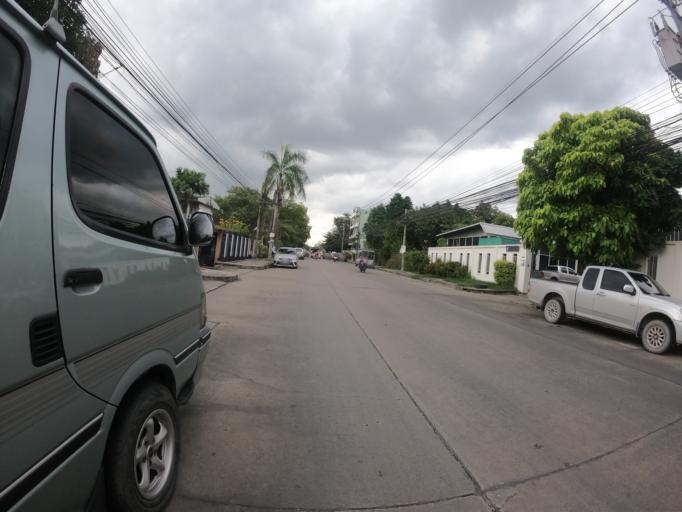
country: TH
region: Bangkok
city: Suan Luang
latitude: 13.7115
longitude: 100.6606
